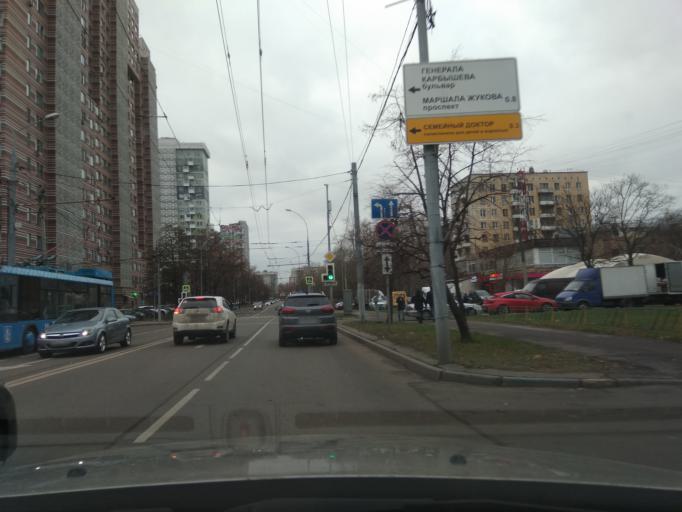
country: RU
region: Moskovskaya
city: Khoroshevo-Mnevniki
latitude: 55.7842
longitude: 37.4724
